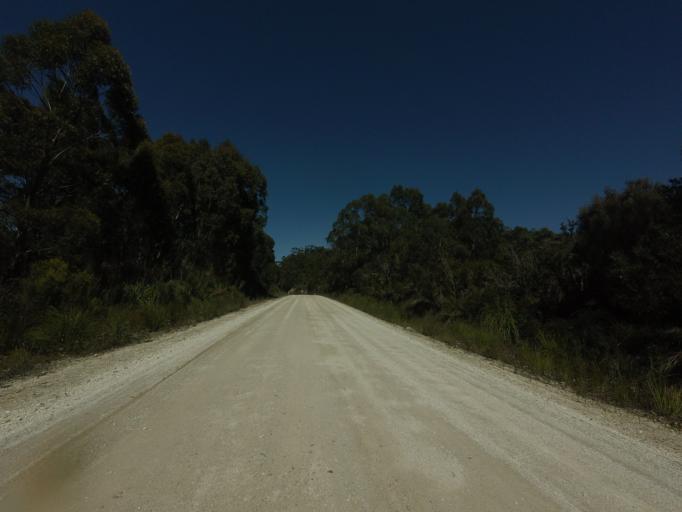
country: AU
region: Tasmania
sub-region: Huon Valley
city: Geeveston
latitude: -42.9021
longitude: 146.3717
